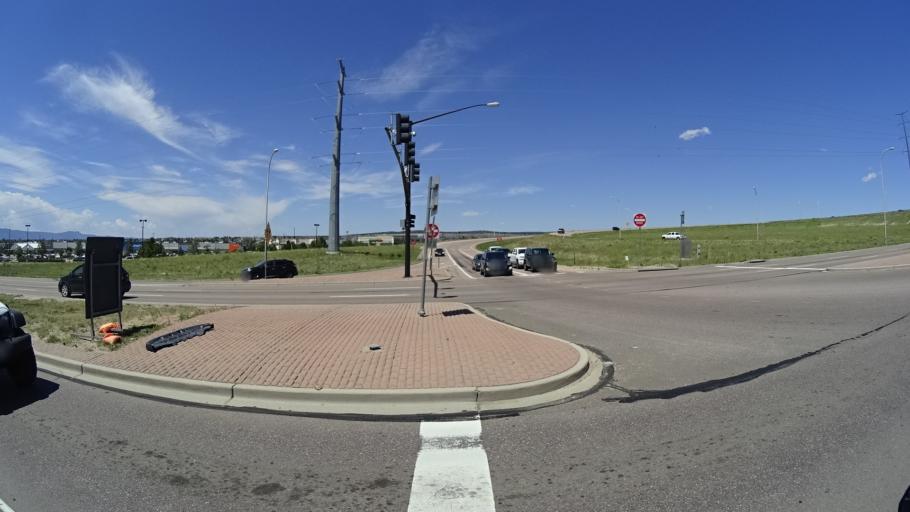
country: US
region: Colorado
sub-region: El Paso County
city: Black Forest
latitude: 38.9400
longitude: -104.7228
